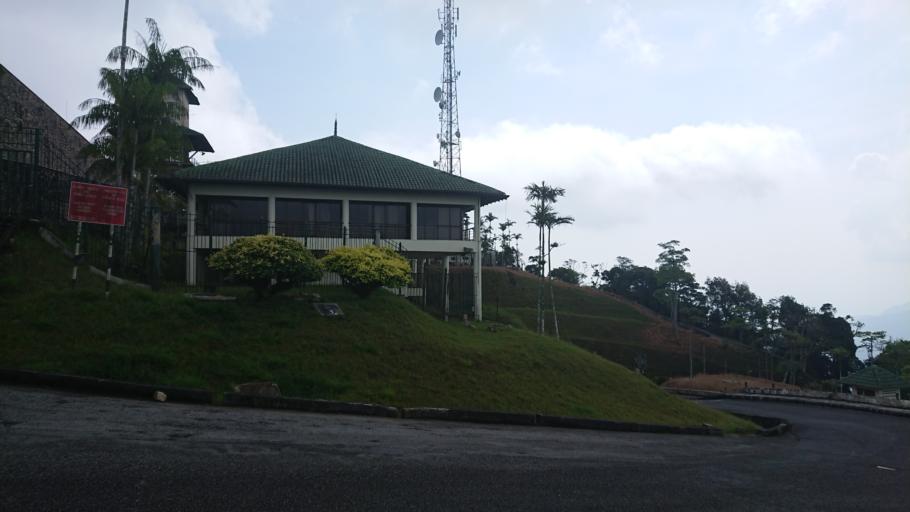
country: MY
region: Kedah
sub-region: Langkawi
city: Kuah
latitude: 6.3696
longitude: 99.8181
